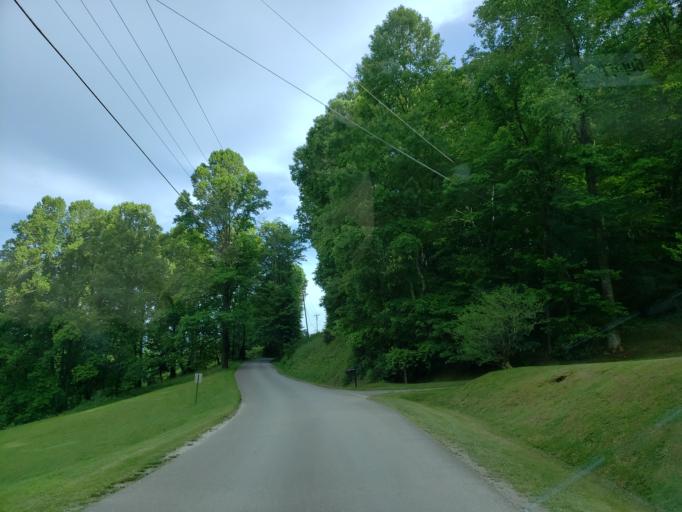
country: US
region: Georgia
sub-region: Fannin County
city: Blue Ridge
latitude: 34.8359
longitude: -84.4114
